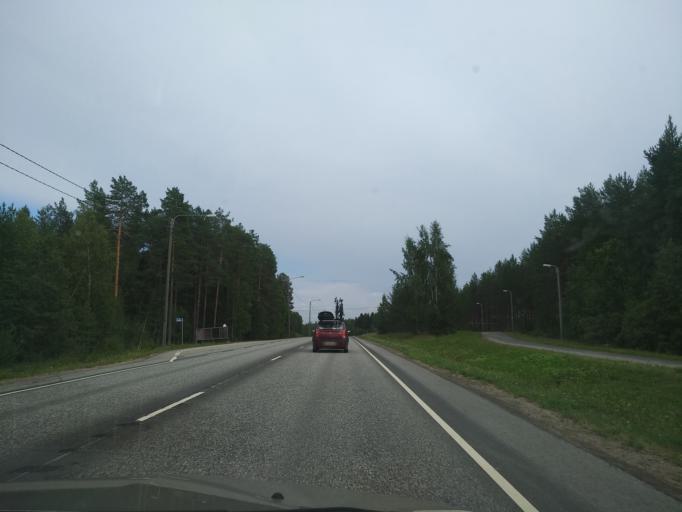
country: FI
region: Kainuu
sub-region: Kajaani
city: Paltamo
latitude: 64.4024
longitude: 27.8685
